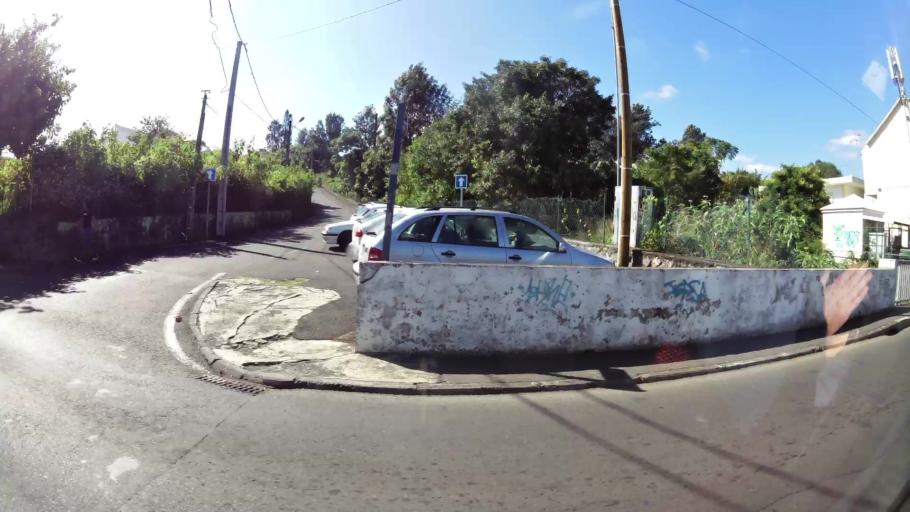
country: RE
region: Reunion
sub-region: Reunion
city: Le Tampon
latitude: -21.2761
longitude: 55.5136
